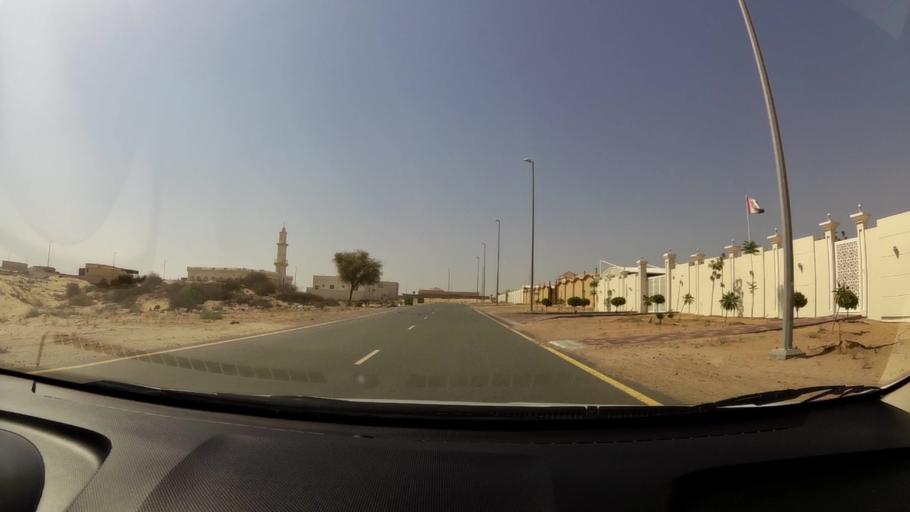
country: AE
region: Umm al Qaywayn
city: Umm al Qaywayn
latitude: 25.4911
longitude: 55.6103
